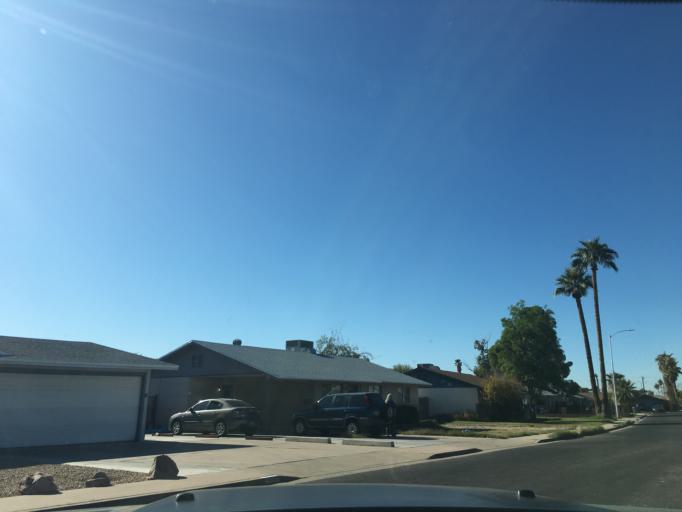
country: US
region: Arizona
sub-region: Maricopa County
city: Mesa
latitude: 33.4466
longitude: -111.8453
